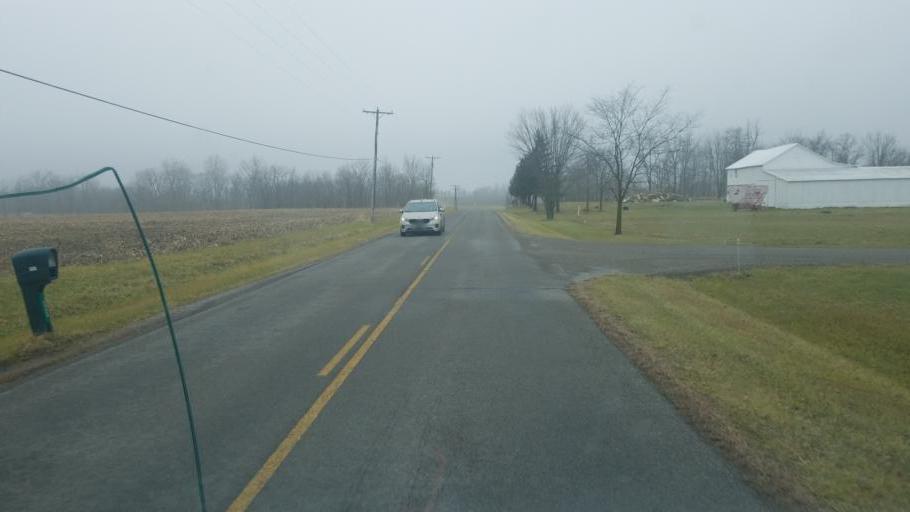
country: US
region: Ohio
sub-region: Champaign County
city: North Lewisburg
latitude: 40.3629
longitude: -83.5511
